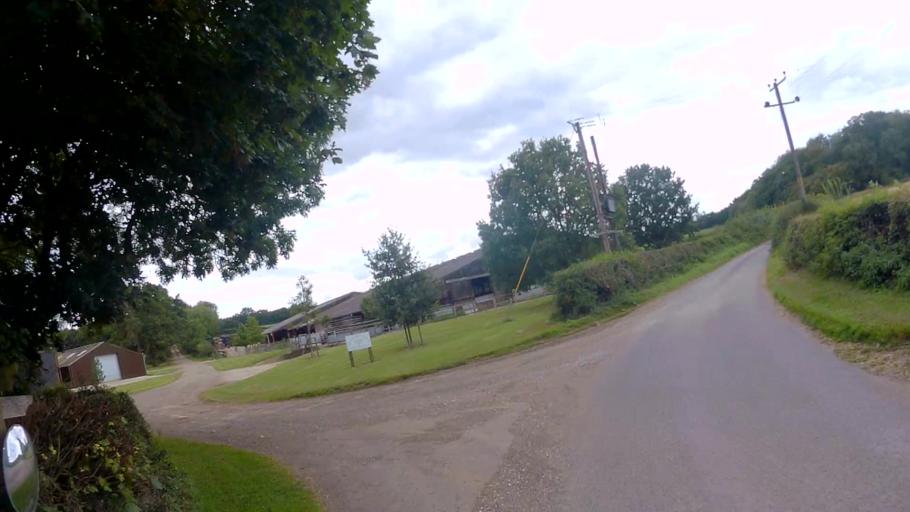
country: GB
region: England
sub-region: Hampshire
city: Overton
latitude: 51.2073
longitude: -1.2337
